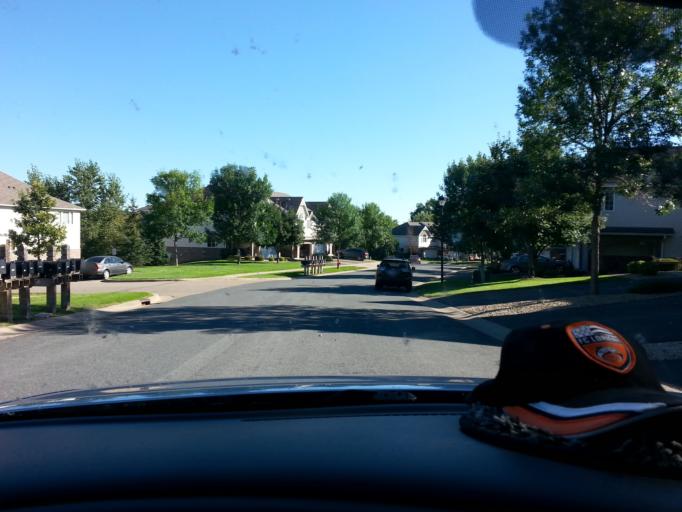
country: US
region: Minnesota
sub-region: Scott County
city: Prior Lake
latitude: 44.7273
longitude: -93.4461
